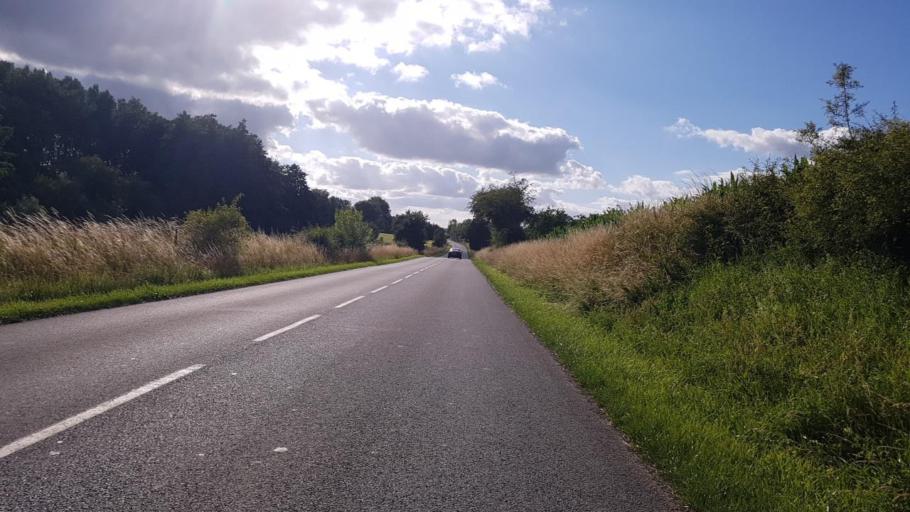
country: FR
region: Picardie
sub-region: Departement de l'Aisne
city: Hirson
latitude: 49.9250
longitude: 4.0466
